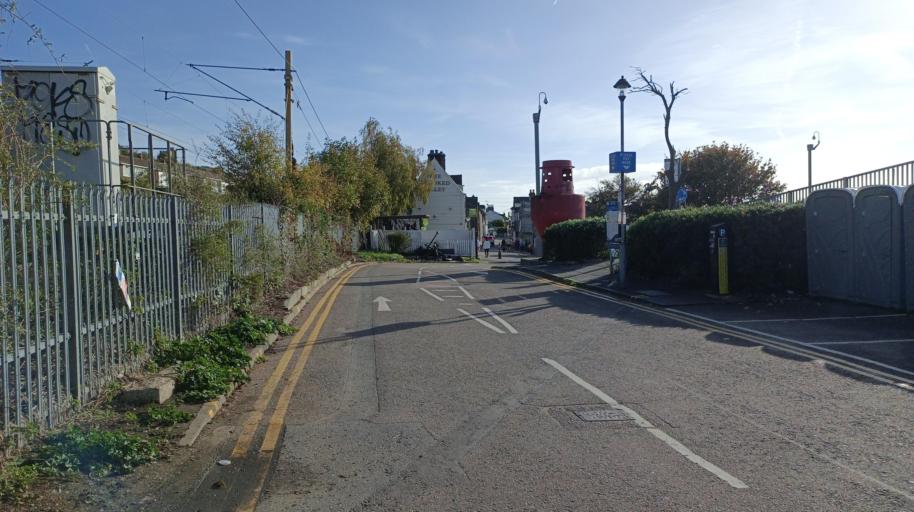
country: GB
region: England
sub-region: Southend-on-Sea
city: Leigh-on-Sea
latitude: 51.5410
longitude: 0.6470
